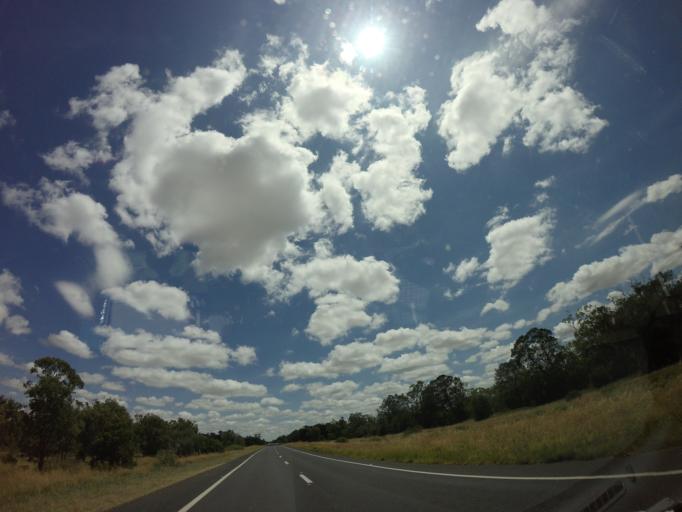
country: AU
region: New South Wales
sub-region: Moree Plains
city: Moree
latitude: -29.1746
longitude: 150.0101
